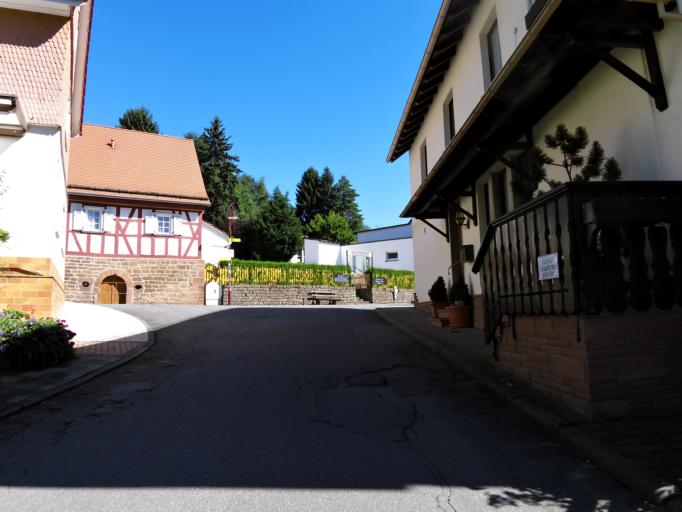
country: DE
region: Hesse
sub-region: Regierungsbezirk Darmstadt
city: Wald-Michelbach
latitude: 49.6272
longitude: 8.8562
